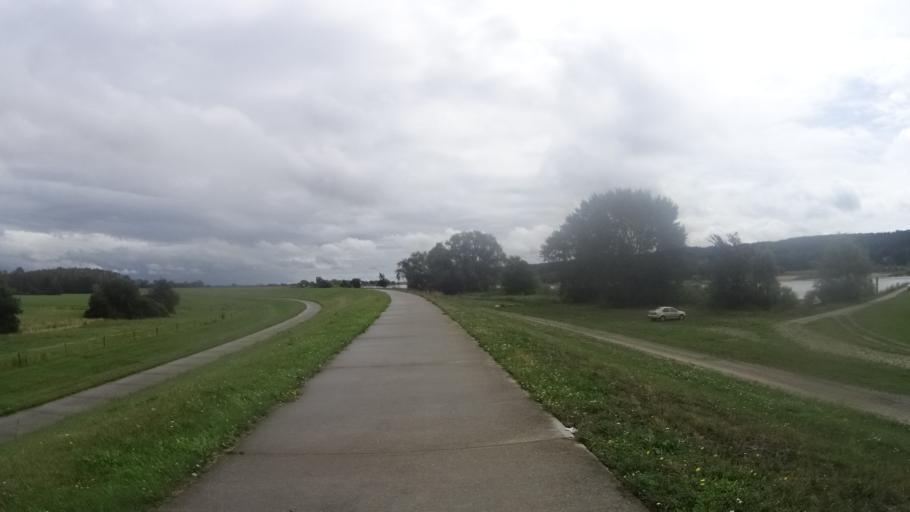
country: DE
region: Lower Saxony
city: Neu Darchau
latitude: 53.2368
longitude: 10.8951
